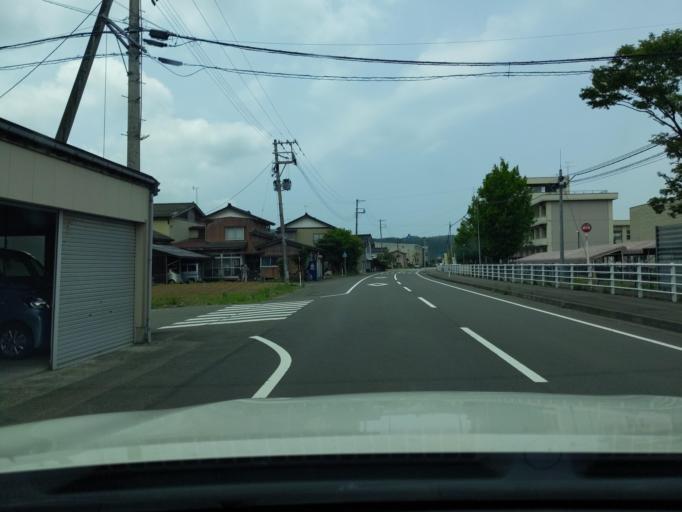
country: JP
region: Niigata
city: Kashiwazaki
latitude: 37.3305
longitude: 138.5674
